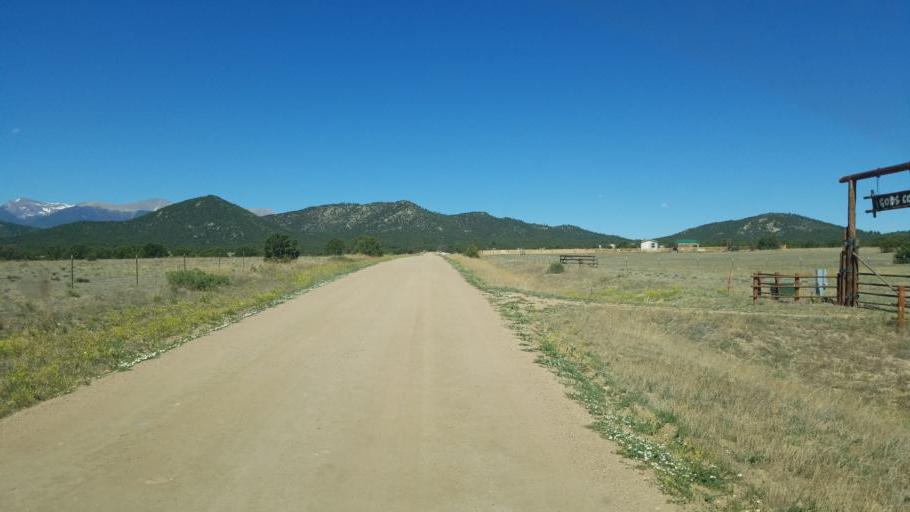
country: US
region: Colorado
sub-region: Custer County
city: Westcliffe
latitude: 38.2851
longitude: -105.5161
